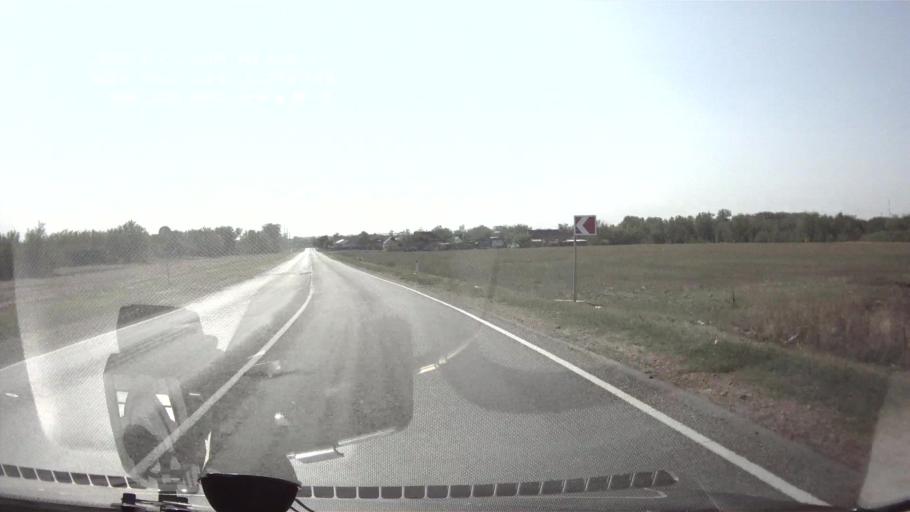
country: RU
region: Krasnodarskiy
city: Dmitriyevskaya
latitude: 45.7403
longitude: 40.7146
